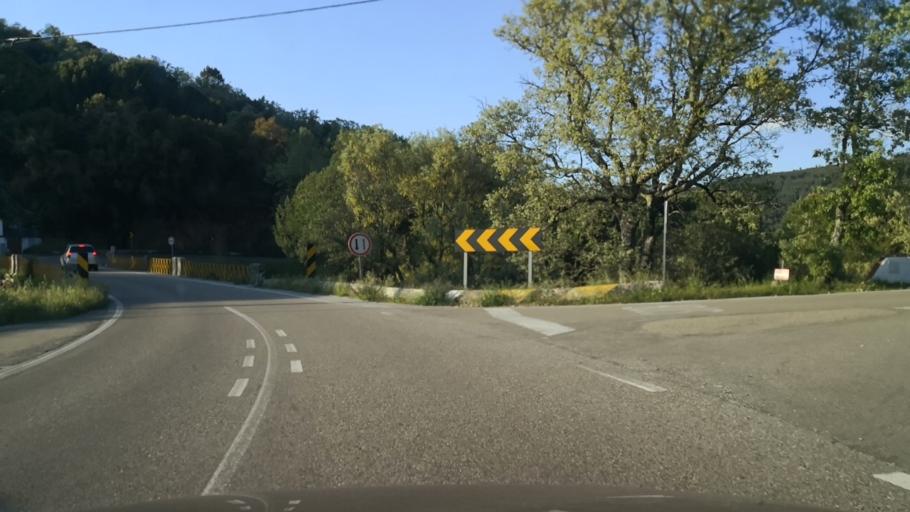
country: PT
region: Portalegre
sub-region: Marvao
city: Marvao
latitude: 39.3660
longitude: -7.3907
